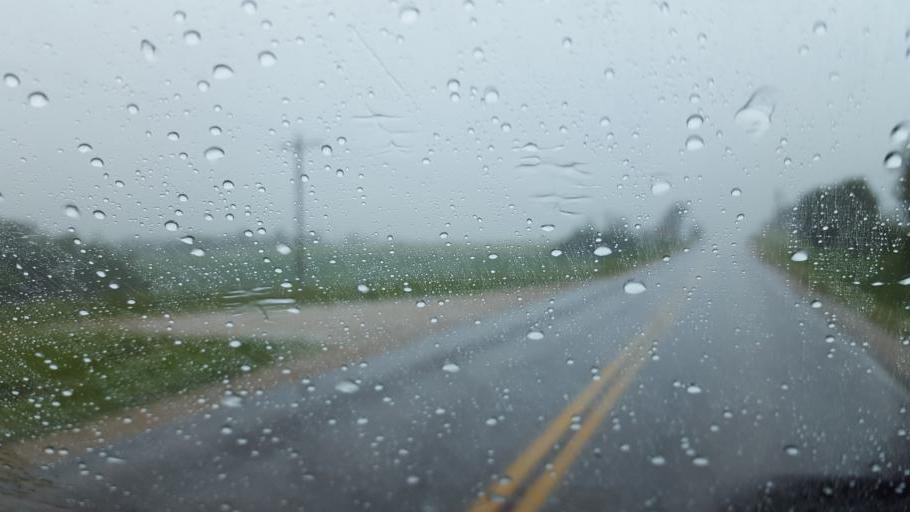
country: US
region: Wisconsin
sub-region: Vernon County
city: Hillsboro
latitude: 43.6200
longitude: -90.4522
